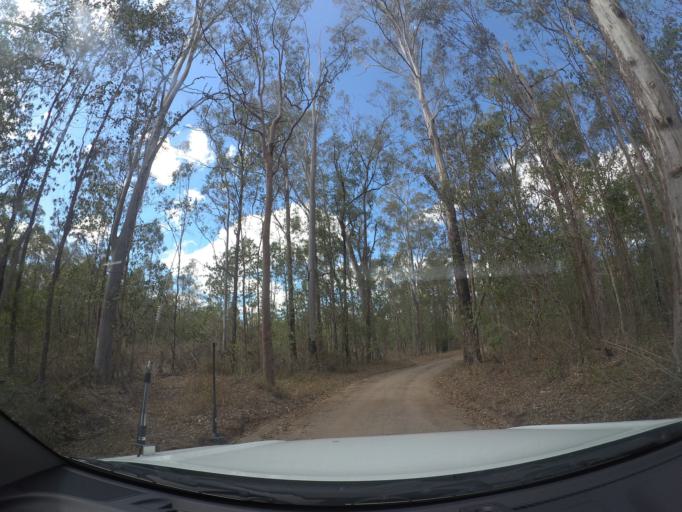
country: AU
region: Queensland
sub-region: Logan
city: North Maclean
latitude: -27.8290
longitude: 152.9679
